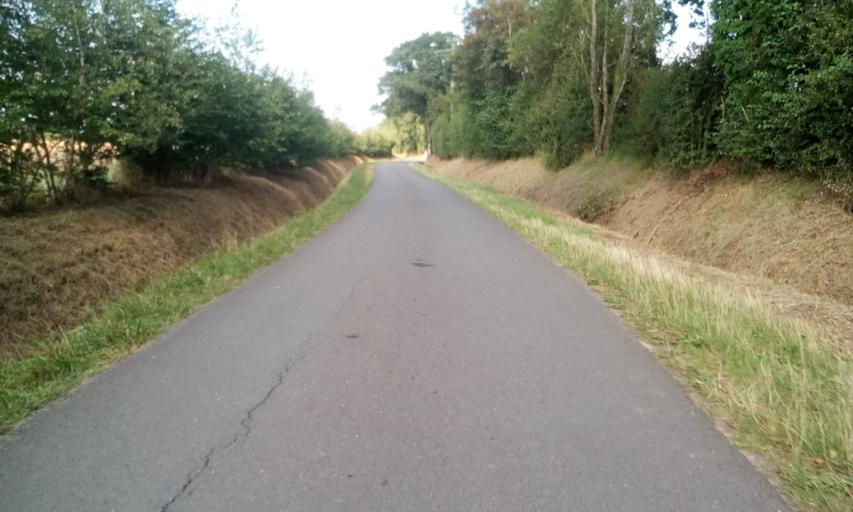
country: FR
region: Lower Normandy
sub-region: Departement du Calvados
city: Argences
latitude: 49.1482
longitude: -0.1253
